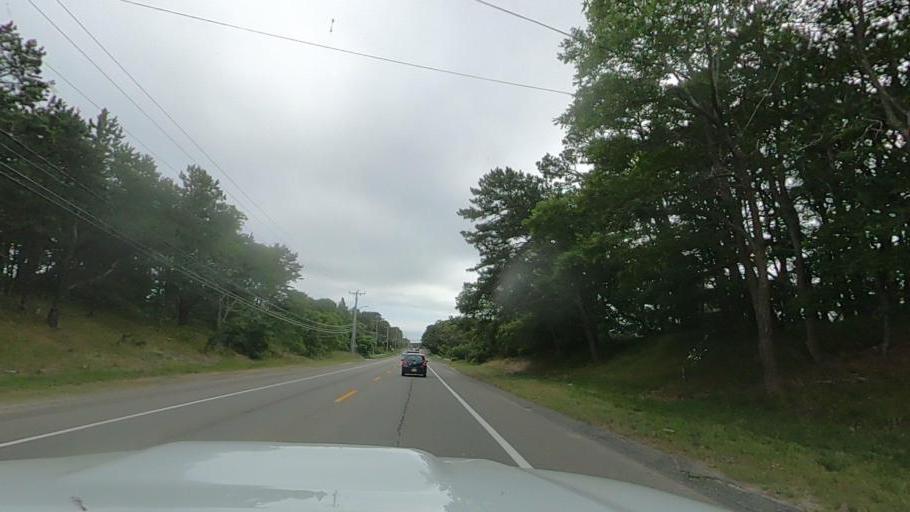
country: US
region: Massachusetts
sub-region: Barnstable County
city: North Eastham
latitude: 41.8972
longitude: -69.9857
